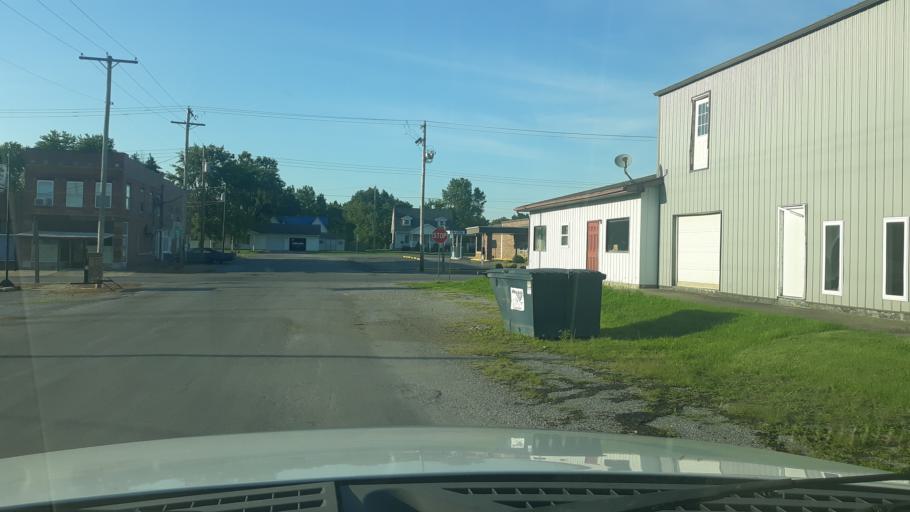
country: US
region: Illinois
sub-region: Saline County
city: Harrisburg
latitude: 37.8403
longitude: -88.6120
